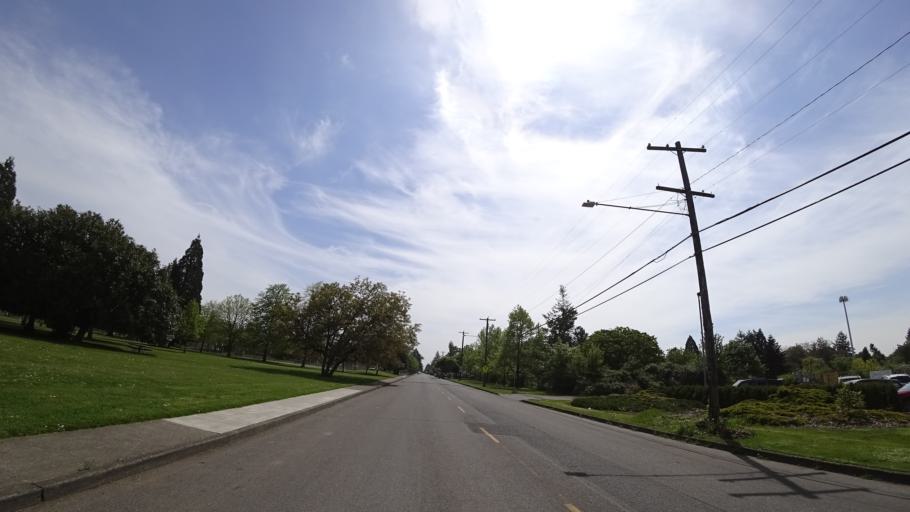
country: US
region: Oregon
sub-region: Multnomah County
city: Lents
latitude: 45.4733
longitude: -122.6022
